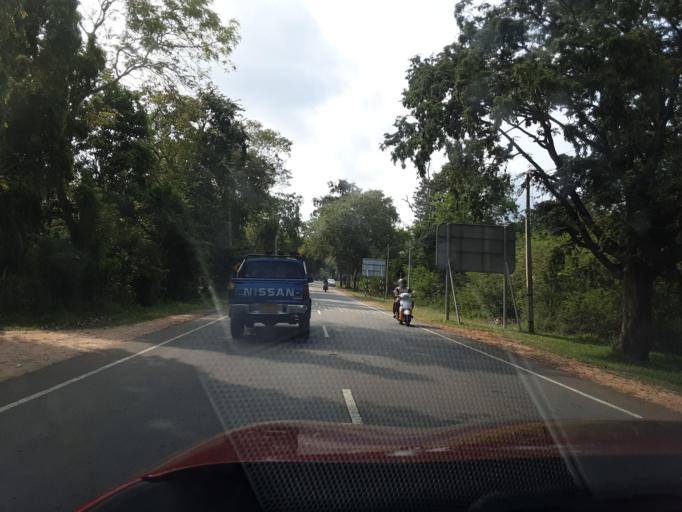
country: LK
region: Uva
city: Haputale
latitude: 6.3619
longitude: 81.1803
